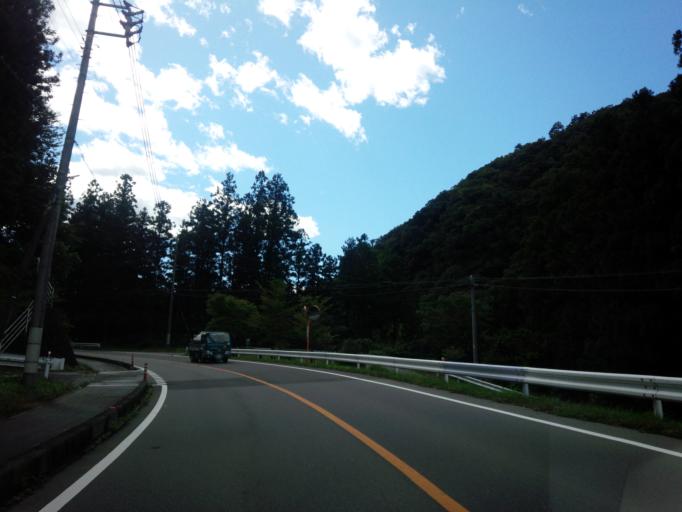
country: JP
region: Gunma
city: Nakanojomachi
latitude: 36.6309
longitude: 138.7941
